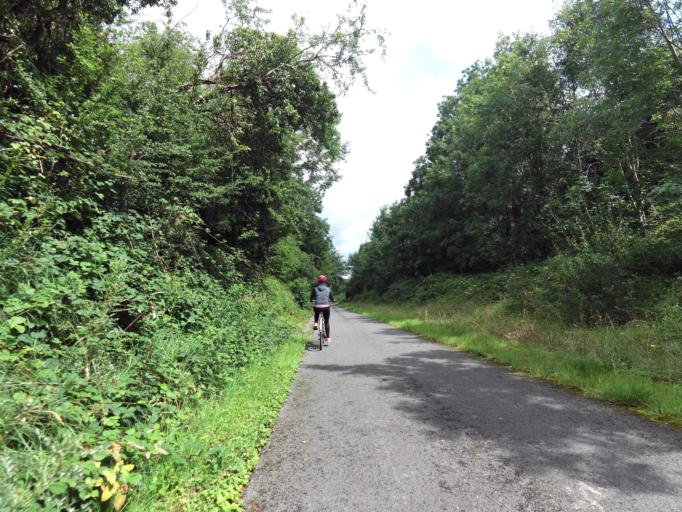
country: IE
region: Leinster
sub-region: An Iarmhi
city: An Muileann gCearr
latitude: 53.4905
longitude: -7.4545
